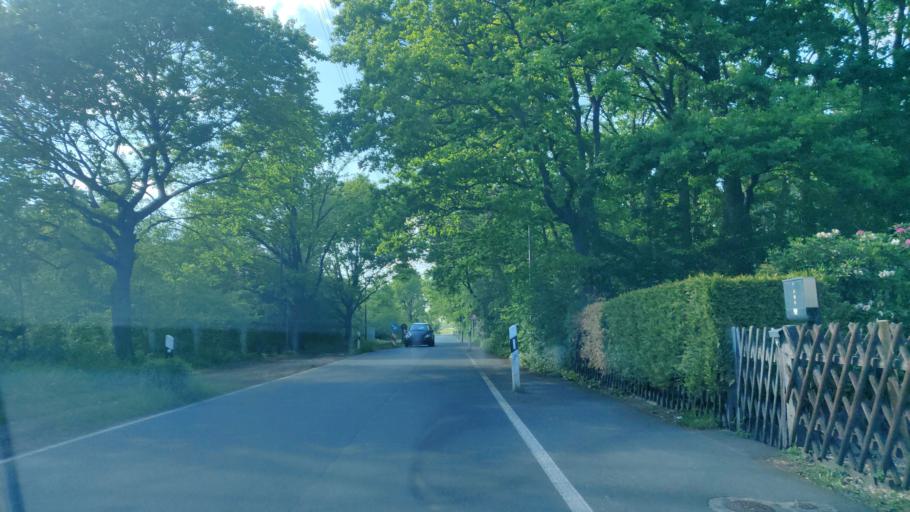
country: DE
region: Lower Saxony
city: Isernhagen Farster Bauerschaft
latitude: 52.4158
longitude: 9.8398
